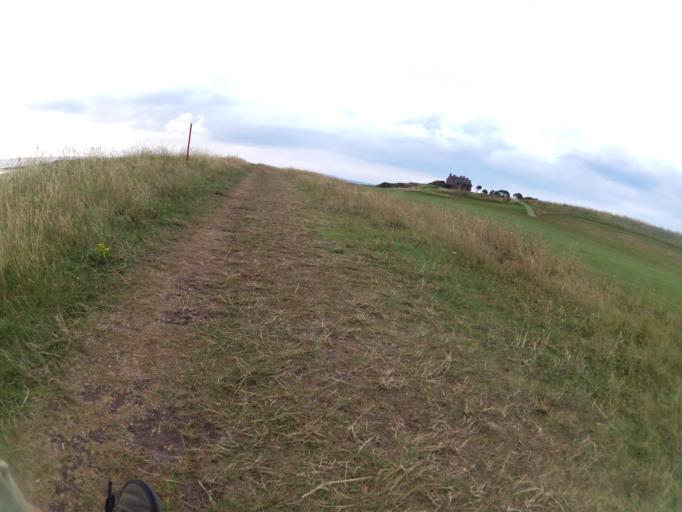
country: GB
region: Scotland
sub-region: East Lothian
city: Dunbar
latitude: 56.0021
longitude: -2.5414
